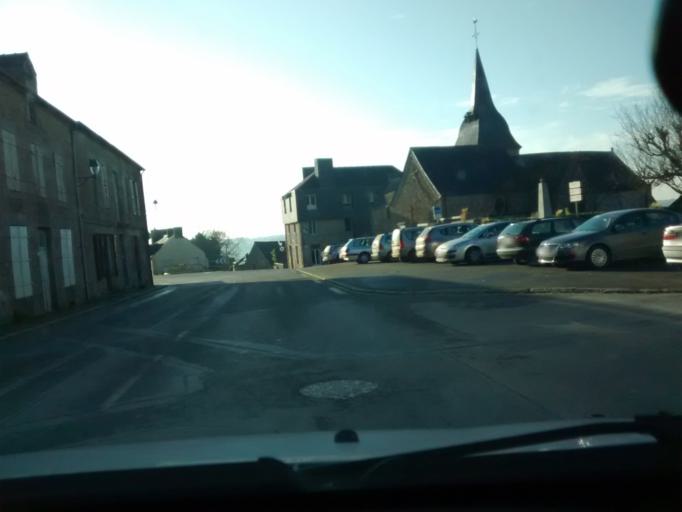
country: FR
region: Brittany
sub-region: Departement d'Ille-et-Vilaine
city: Tremblay
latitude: 48.3761
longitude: -1.4970
